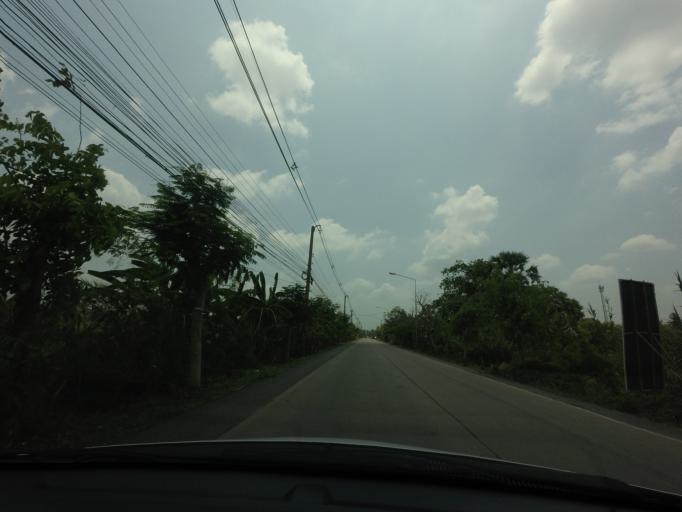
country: TH
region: Pathum Thani
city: Sam Khok
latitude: 14.0442
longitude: 100.5303
